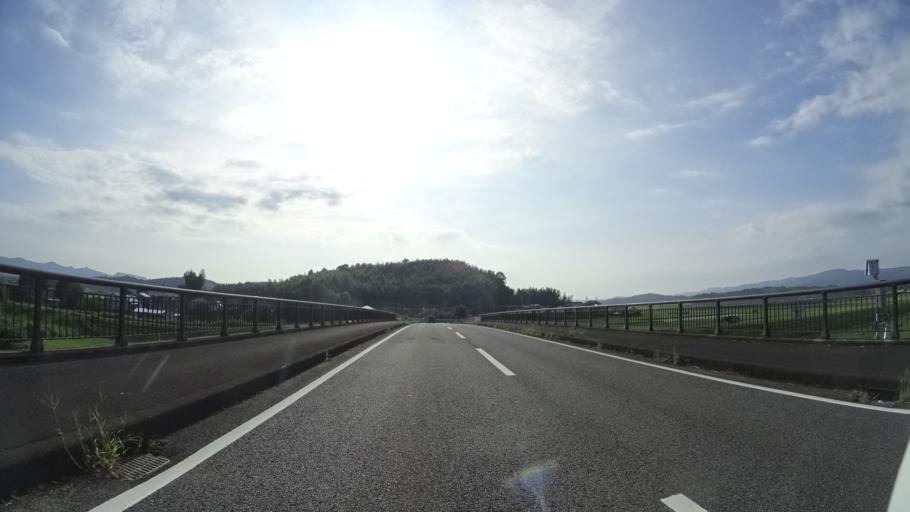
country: JP
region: Kagoshima
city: Okuchi-shinohara
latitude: 32.0269
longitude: 130.6019
